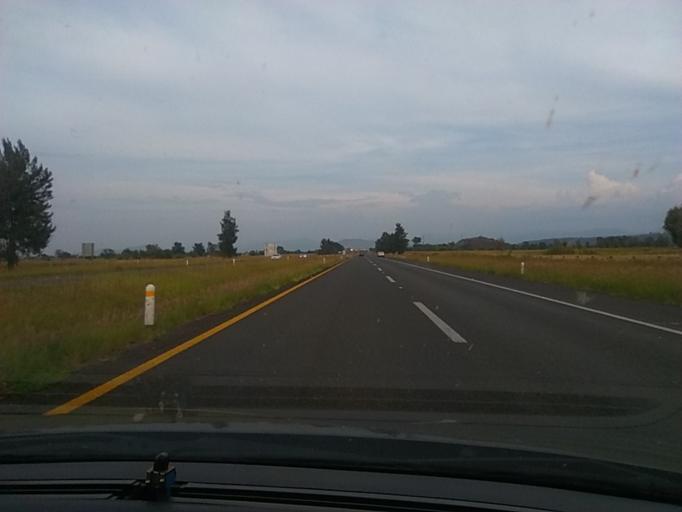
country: MX
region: Michoacan
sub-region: Alvaro Obregon
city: Tzintzimeo
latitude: 19.8913
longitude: -100.9965
